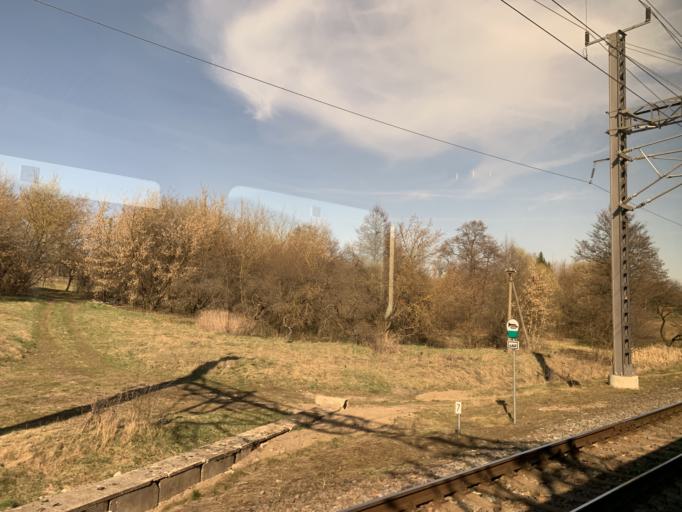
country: LT
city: Skaidiskes
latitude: 54.6966
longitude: 25.4318
